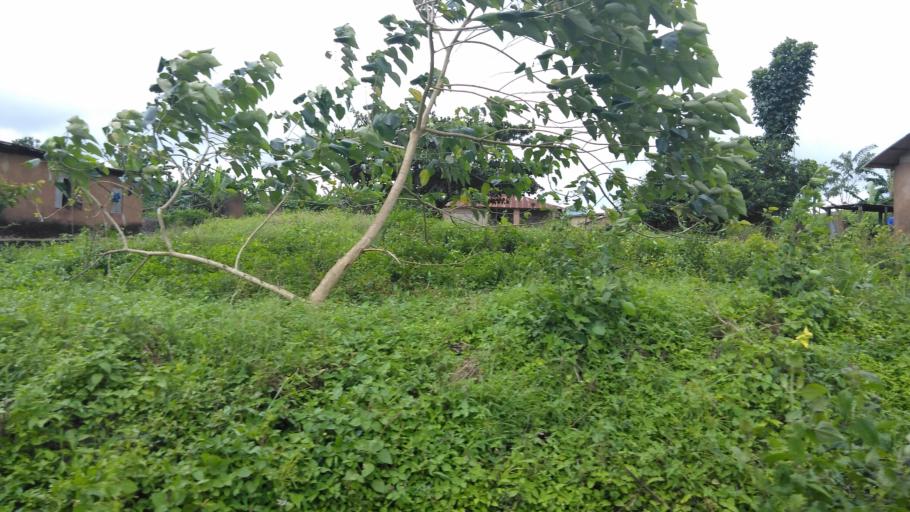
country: NG
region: Ogun
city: Abigi
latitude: 6.5987
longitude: 4.4894
